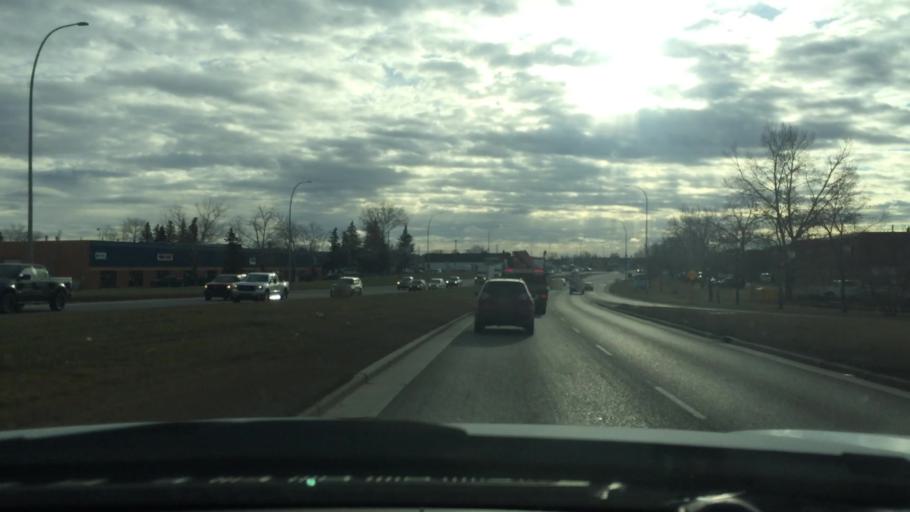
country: CA
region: Alberta
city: Calgary
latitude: 51.0016
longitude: -113.9882
